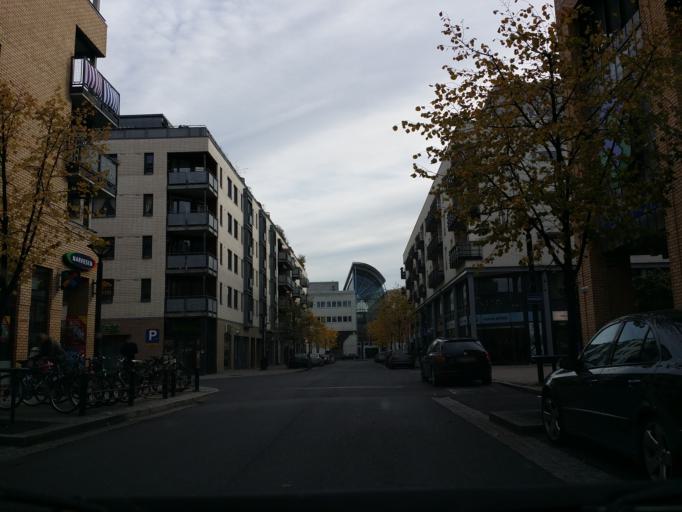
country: NO
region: Akershus
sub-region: Baerum
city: Sandvika
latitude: 59.8902
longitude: 10.5217
